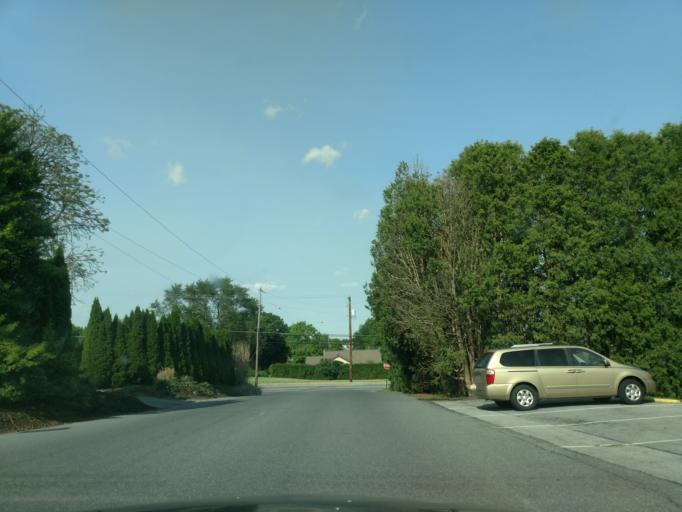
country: US
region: Pennsylvania
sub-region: Lebanon County
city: Lebanon South
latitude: 40.3253
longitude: -76.4047
